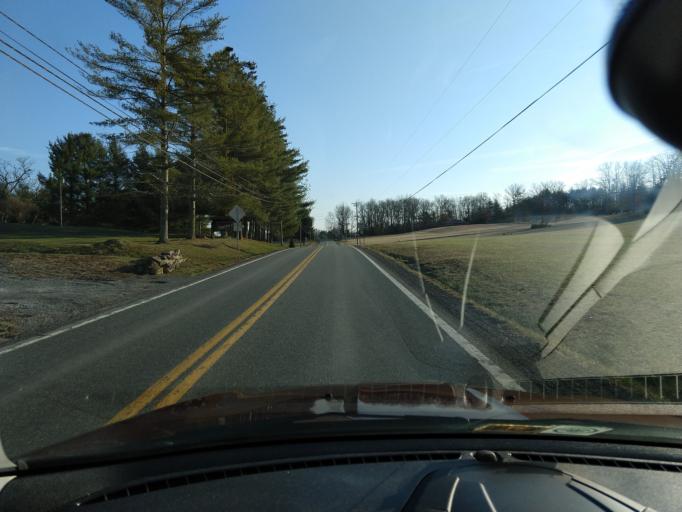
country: US
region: West Virginia
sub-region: Pocahontas County
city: Marlinton
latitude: 38.2011
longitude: -80.1130
